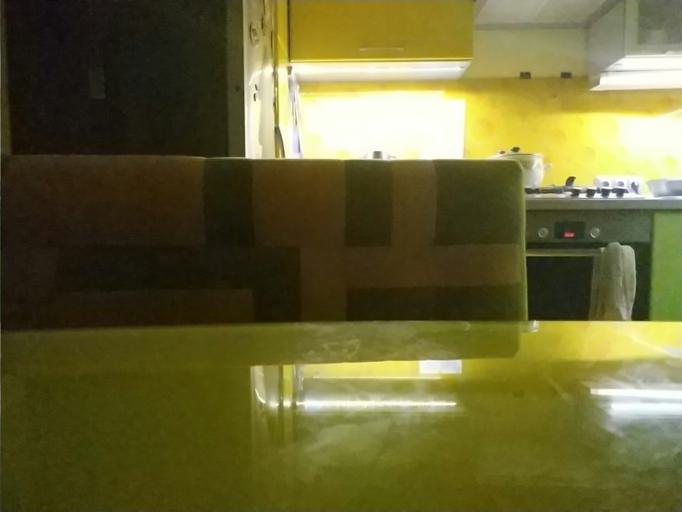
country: RU
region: Republic of Karelia
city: Kalevala
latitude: 65.3322
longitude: 30.6868
